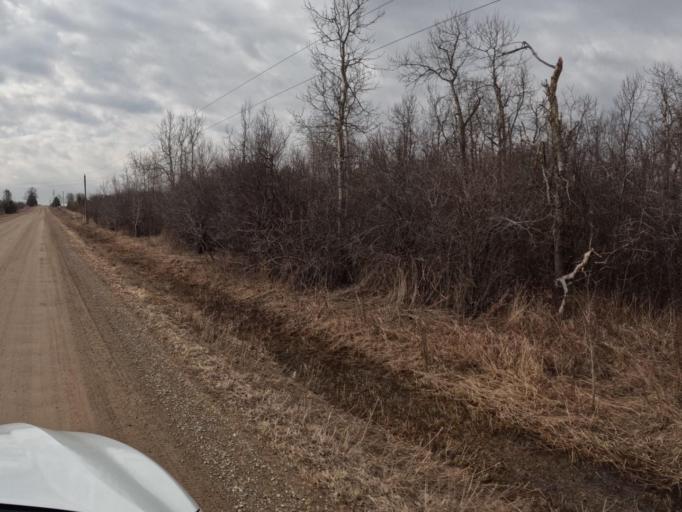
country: CA
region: Ontario
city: Orangeville
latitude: 43.9348
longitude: -80.1890
